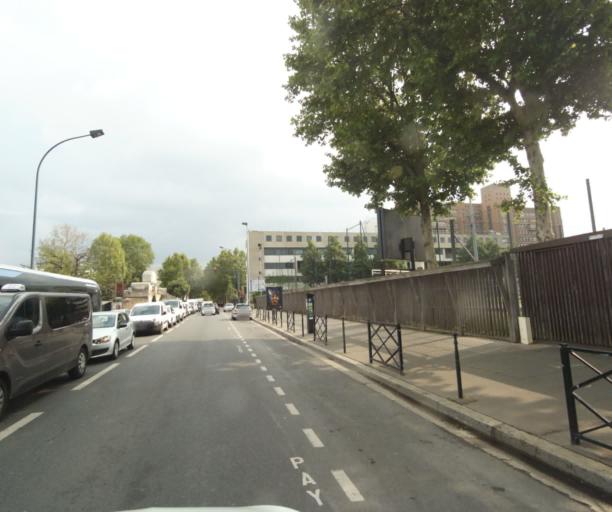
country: FR
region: Ile-de-France
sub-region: Departement des Hauts-de-Seine
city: Clichy
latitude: 48.9096
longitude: 2.3129
